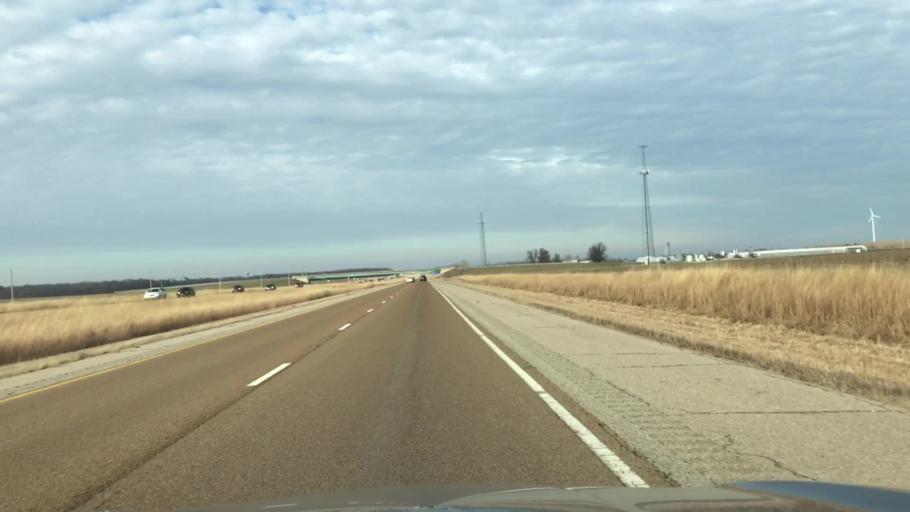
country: US
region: Illinois
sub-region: Montgomery County
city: Raymond
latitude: 39.4157
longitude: -89.6432
